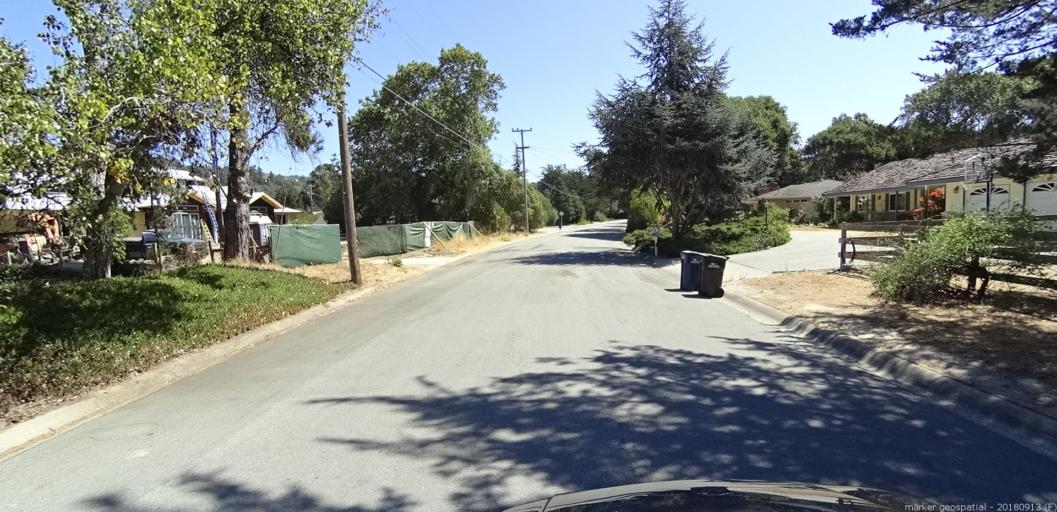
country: US
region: California
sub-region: Monterey County
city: Carmel-by-the-Sea
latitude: 36.5380
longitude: -121.8672
